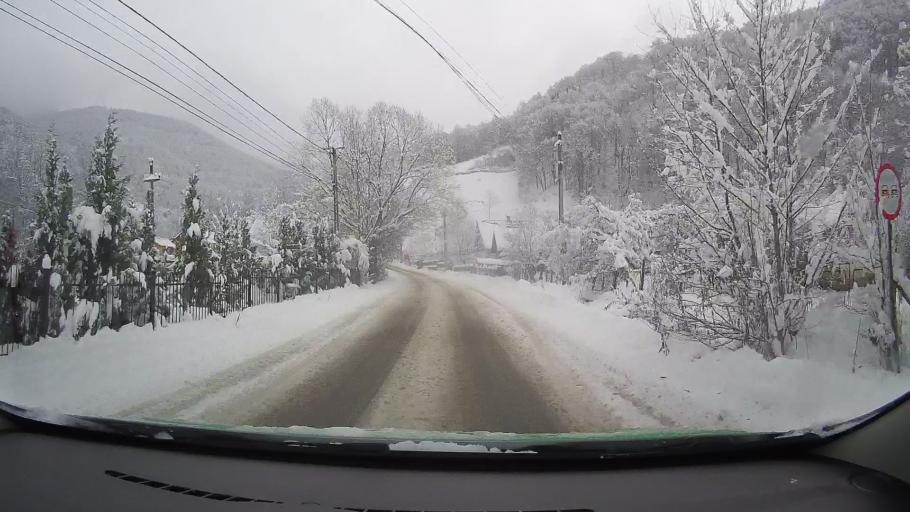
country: RO
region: Alba
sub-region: Comuna Sugag
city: Dobra
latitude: 45.7632
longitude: 23.6521
